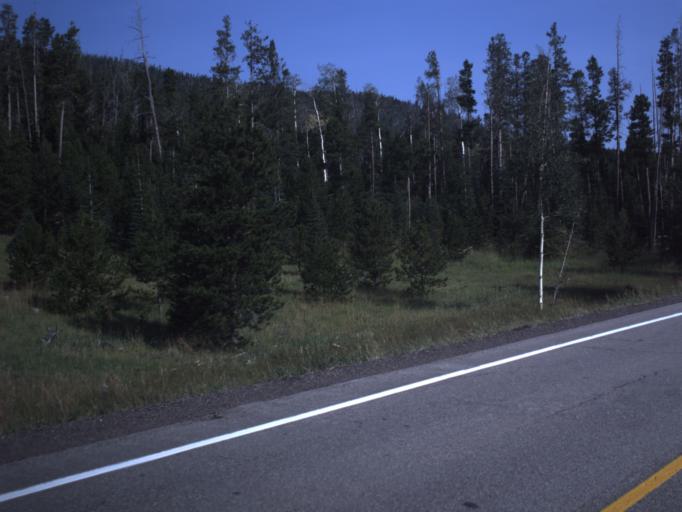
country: US
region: Utah
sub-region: Daggett County
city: Manila
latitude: 40.8312
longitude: -109.4632
